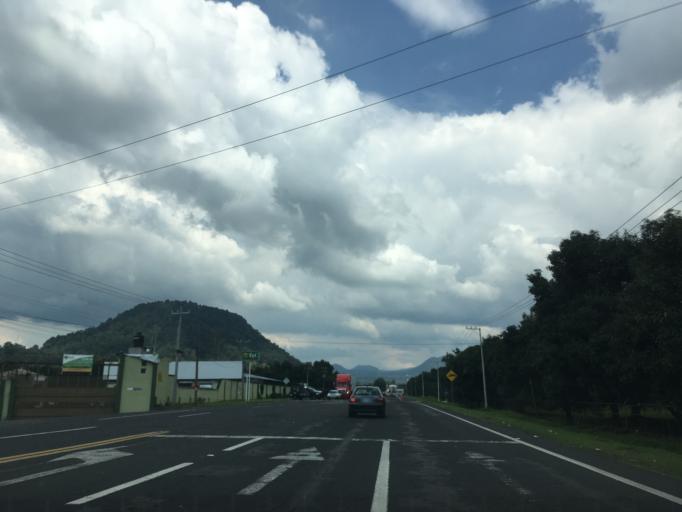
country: MX
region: Michoacan
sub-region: Uruapan
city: Uruapan
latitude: 19.4508
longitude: -102.0763
